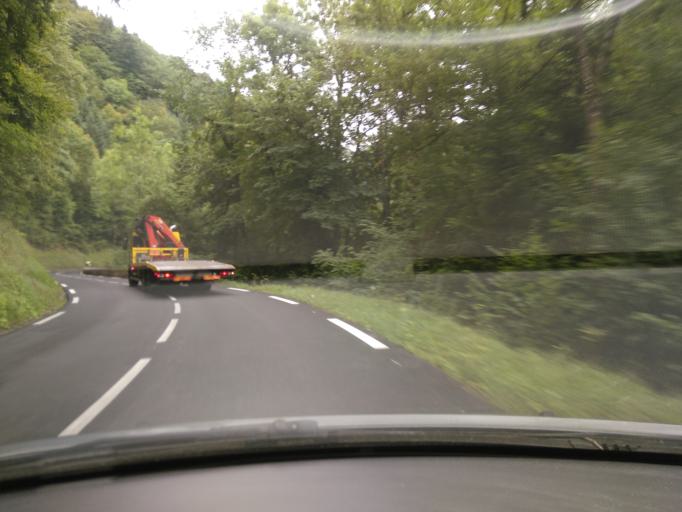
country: FR
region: Rhone-Alpes
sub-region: Departement de la Haute-Savoie
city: Bonneville
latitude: 46.0395
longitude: 6.3810
